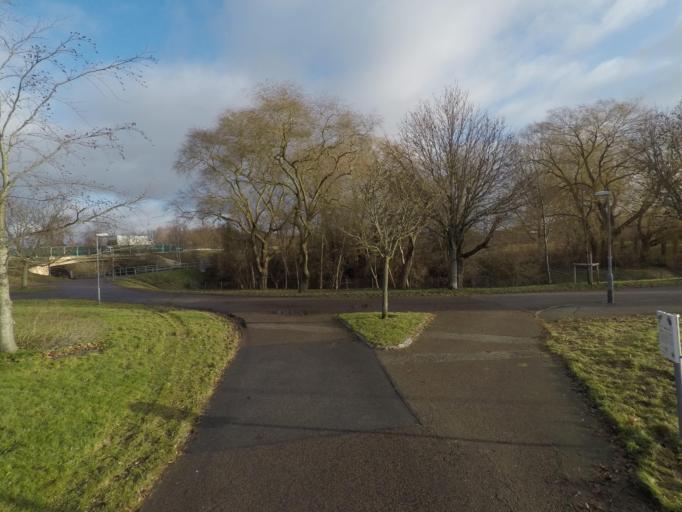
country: SE
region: Skane
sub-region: Burlovs Kommun
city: Arloev
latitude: 55.5938
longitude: 13.0809
